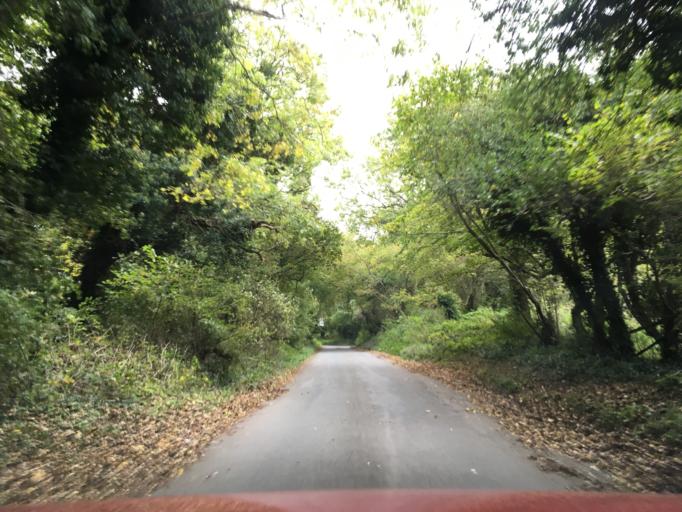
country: GB
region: England
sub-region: South Gloucestershire
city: Horton
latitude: 51.5880
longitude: -2.3348
